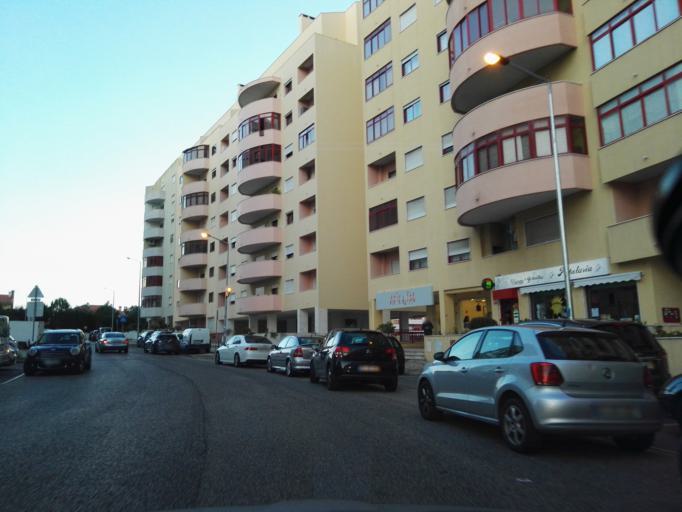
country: PT
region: Lisbon
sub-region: Vila Franca de Xira
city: Vialonga
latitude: 38.8667
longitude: -9.0652
